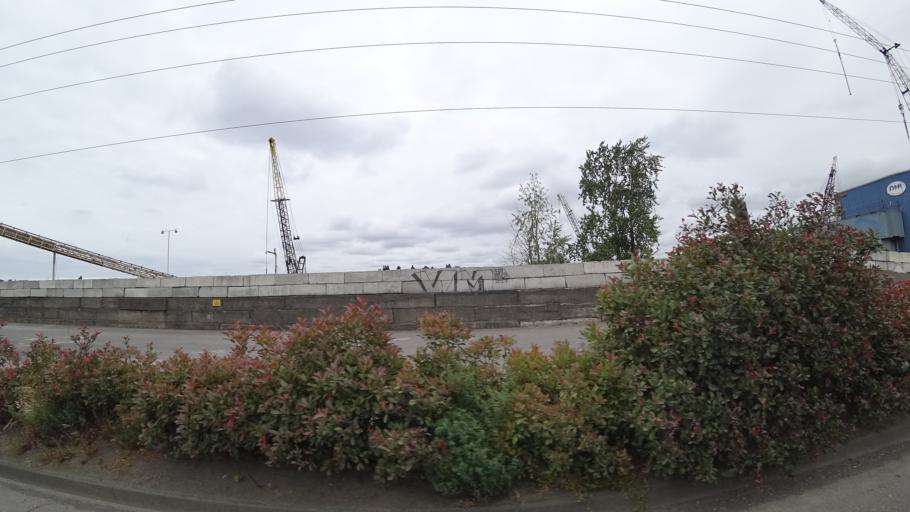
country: US
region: Washington
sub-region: Clark County
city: Vancouver
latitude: 45.6075
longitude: -122.6859
